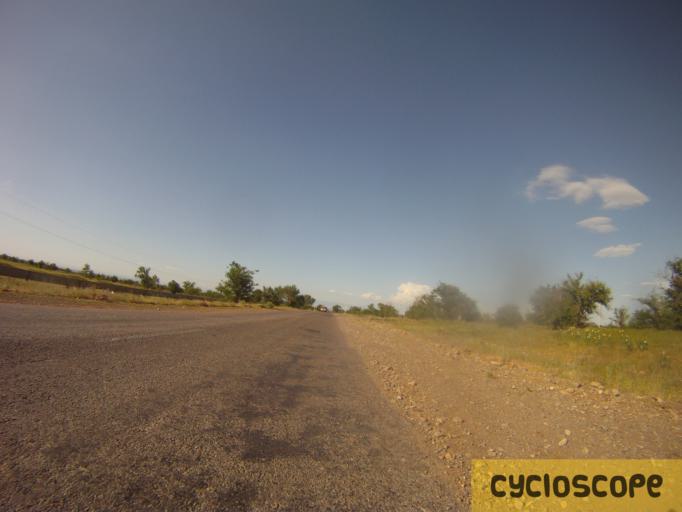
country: KZ
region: Almaty Oblysy
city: Turgen'
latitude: 43.4473
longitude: 77.6220
